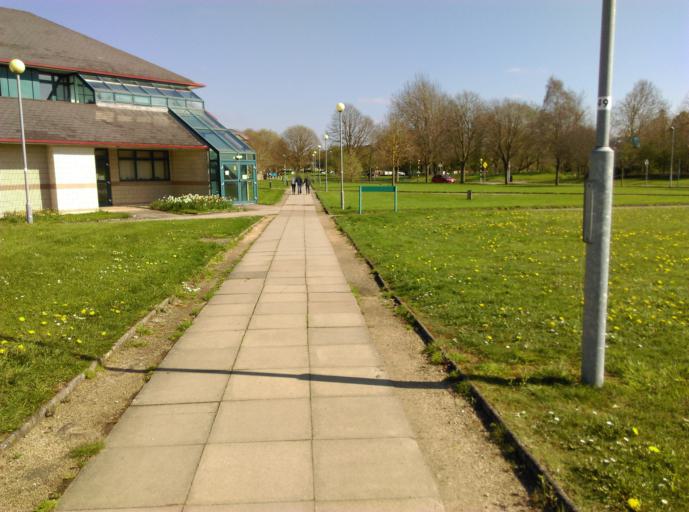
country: IE
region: Leinster
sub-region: Kildare
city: Maynooth
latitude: 53.3830
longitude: -6.6018
